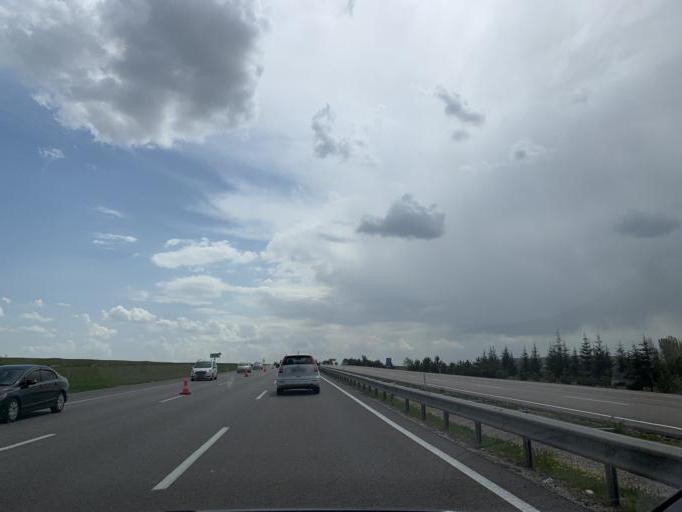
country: TR
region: Ankara
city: Polatli
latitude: 39.6229
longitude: 32.1914
